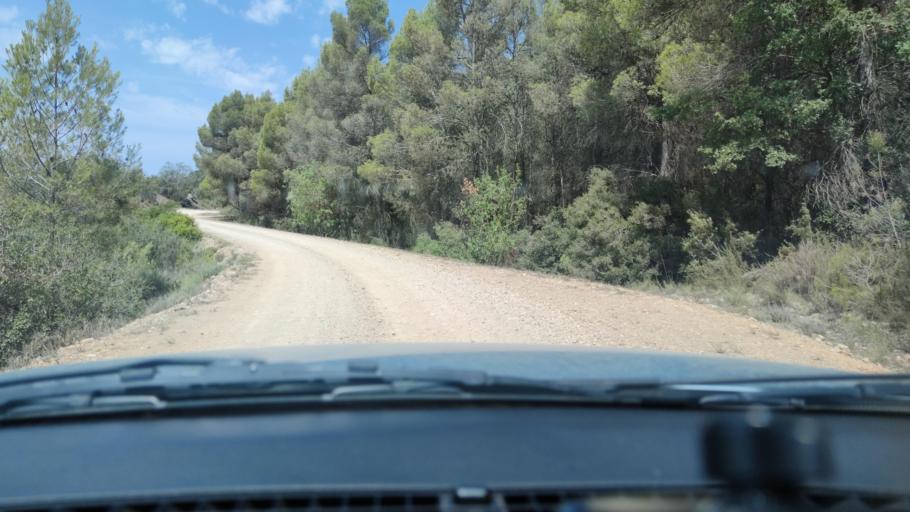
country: ES
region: Catalonia
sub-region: Provincia de Lleida
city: Camarasa
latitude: 41.9260
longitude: 0.8389
